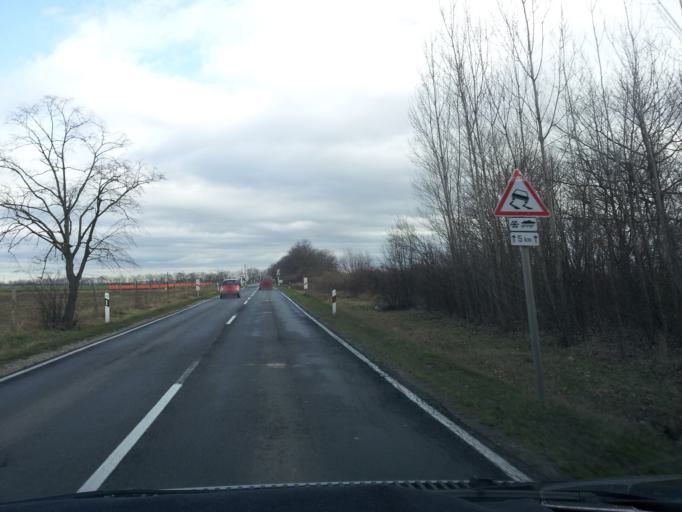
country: HU
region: Vas
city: Gencsapati
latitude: 47.2754
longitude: 16.6093
